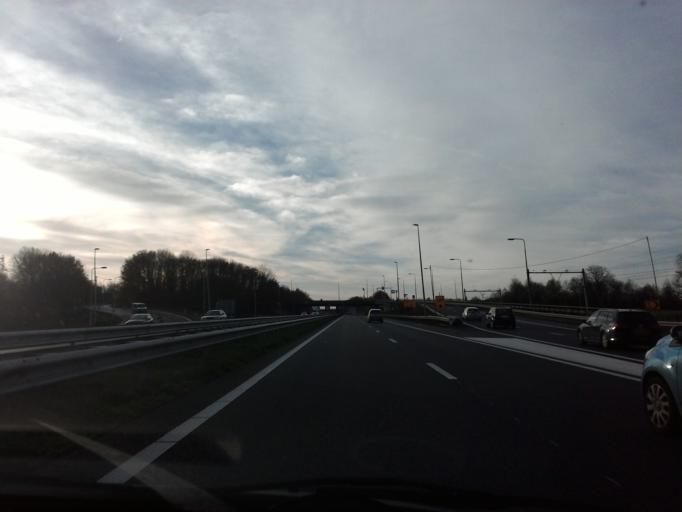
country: NL
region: Limburg
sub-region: Gemeente Maastricht
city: Heer
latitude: 50.8337
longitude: 5.7183
